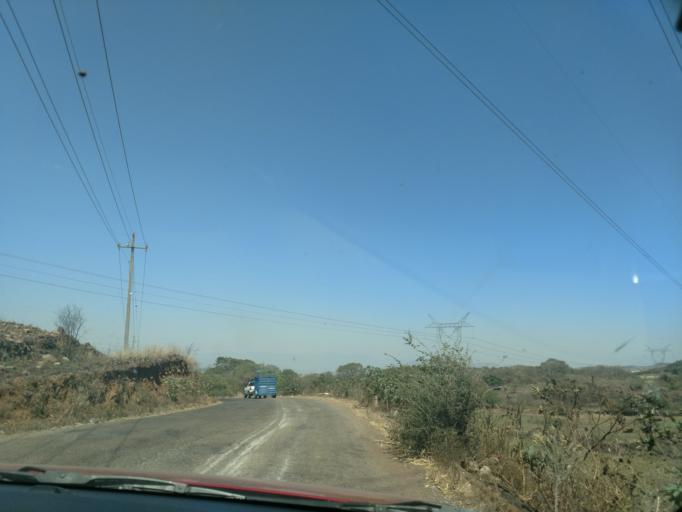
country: MX
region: Nayarit
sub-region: Tepic
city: La Corregidora
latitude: 21.5018
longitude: -104.7368
